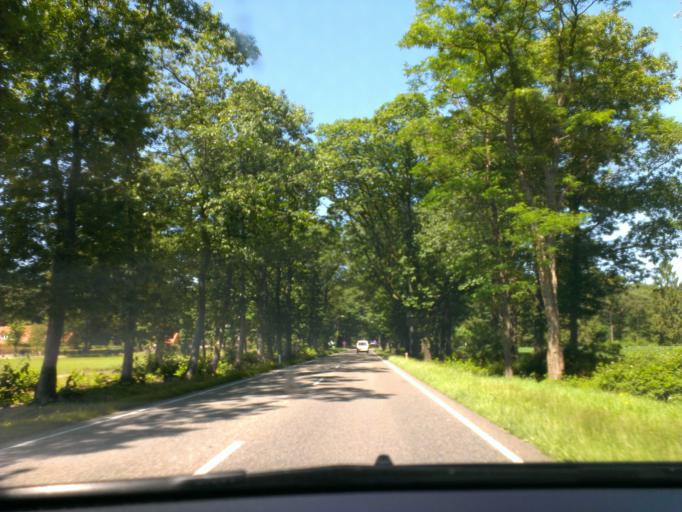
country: NL
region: Gelderland
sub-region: Gemeente Heerde
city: Heerde
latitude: 52.4025
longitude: 6.0245
